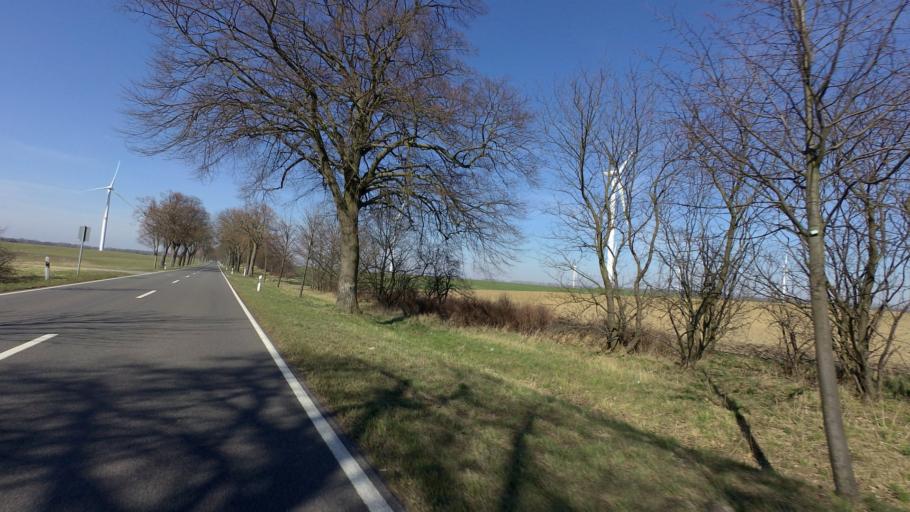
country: DE
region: Brandenburg
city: Eberswalde
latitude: 52.7557
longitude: 13.8422
